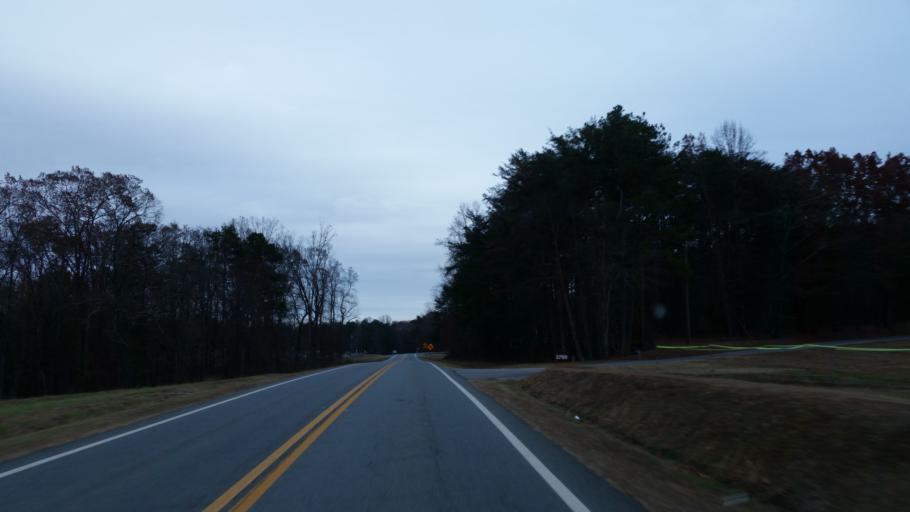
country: US
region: Georgia
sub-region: Dawson County
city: Dawsonville
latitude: 34.4560
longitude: -84.1379
